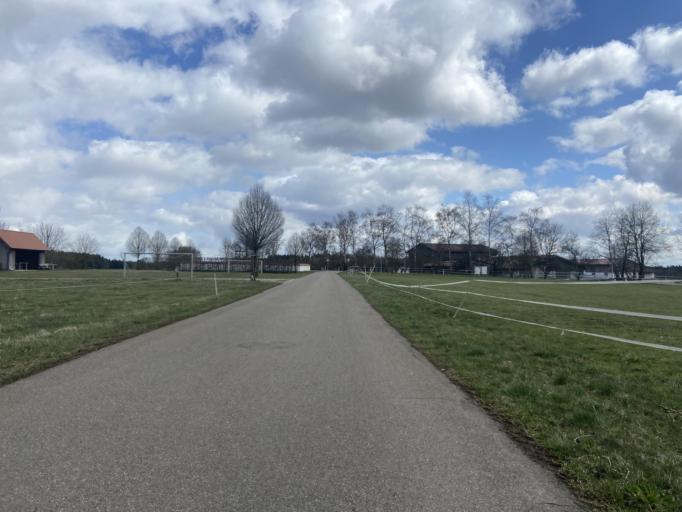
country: DE
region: Baden-Wuerttemberg
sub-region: Tuebingen Region
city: Veringenstadt
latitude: 48.1509
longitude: 9.2436
